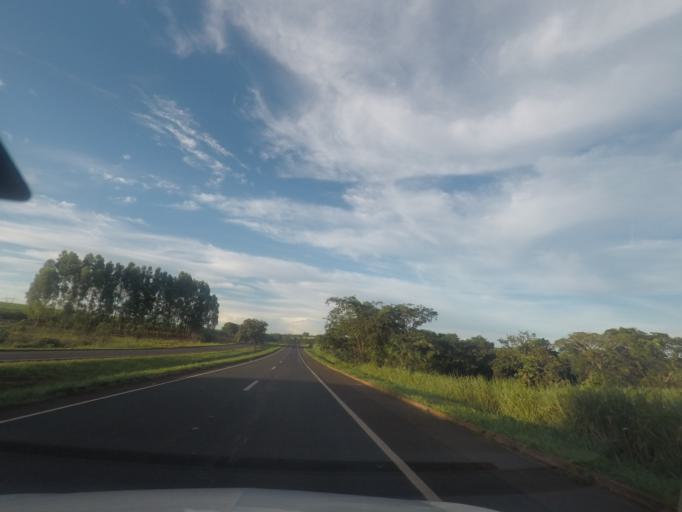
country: BR
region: Goias
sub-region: Goiatuba
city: Goiatuba
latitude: -18.0174
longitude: -49.2630
